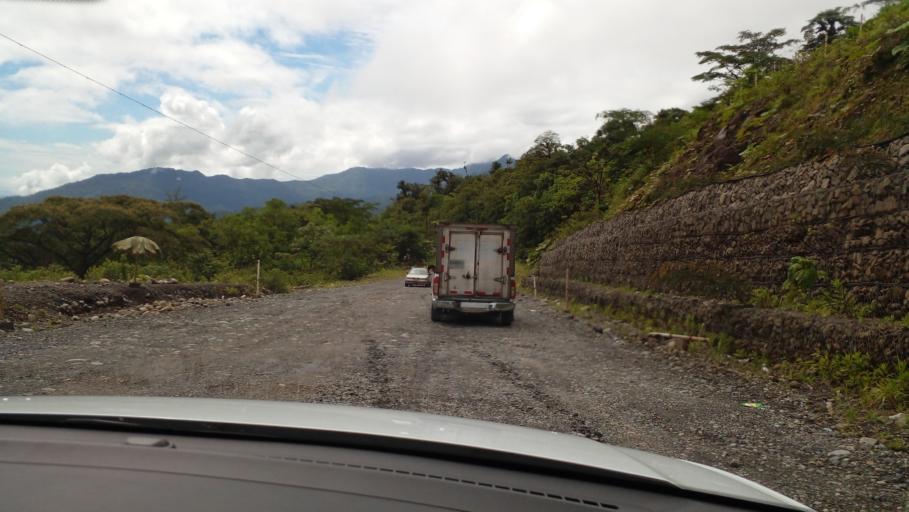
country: PA
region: Bocas del Toro
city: Chiriqui Grande
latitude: 8.7802
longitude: -82.2066
